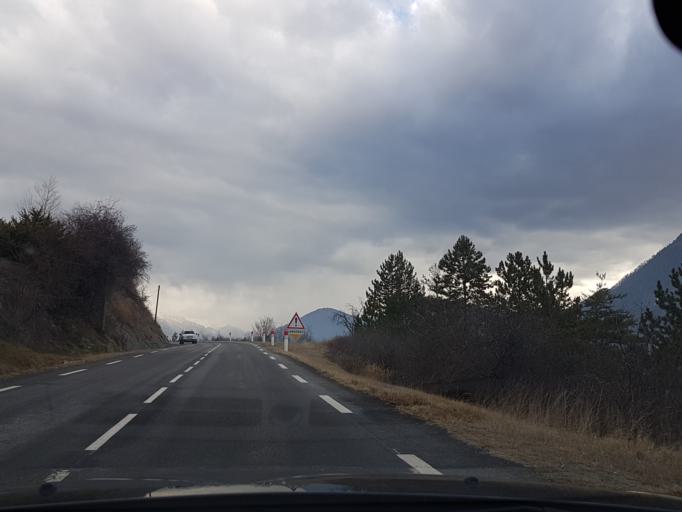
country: FR
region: Provence-Alpes-Cote d'Azur
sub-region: Departement des Hautes-Alpes
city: Tallard
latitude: 44.4679
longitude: 6.1406
